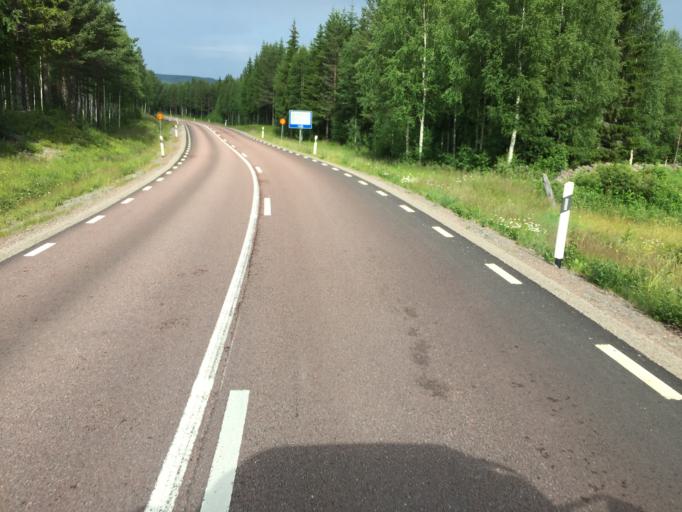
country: SE
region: Dalarna
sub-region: Vansbro Kommun
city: Vansbro
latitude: 60.8170
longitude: 14.1166
